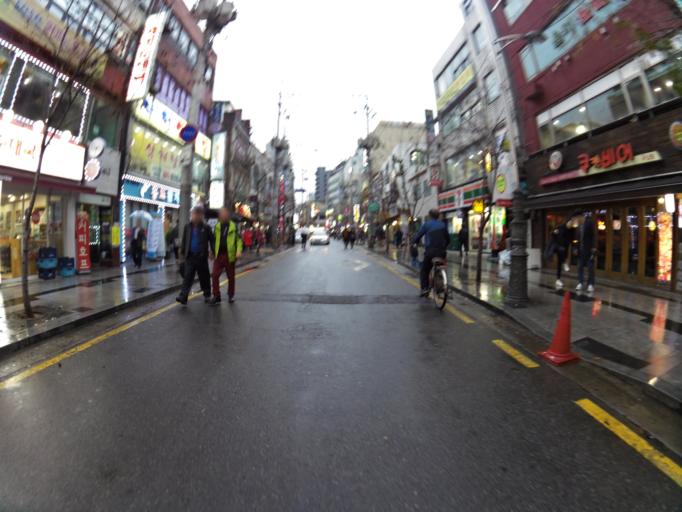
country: KR
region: Seoul
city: Seoul
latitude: 37.5707
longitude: 126.9897
